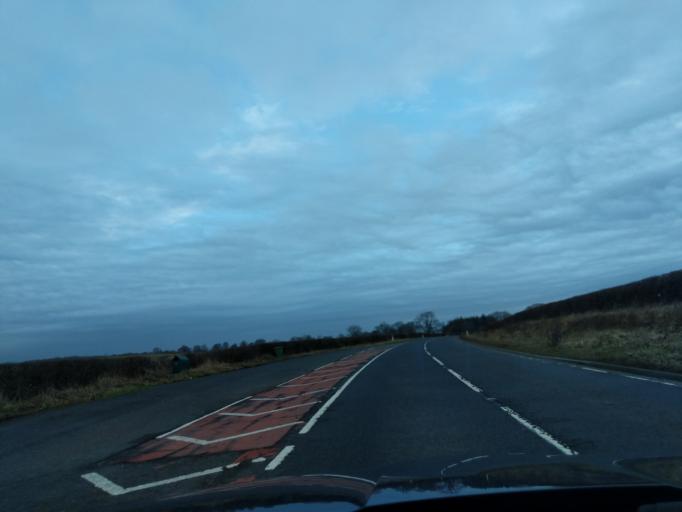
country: GB
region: England
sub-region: Northumberland
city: Rothley
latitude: 55.1231
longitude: -1.9224
